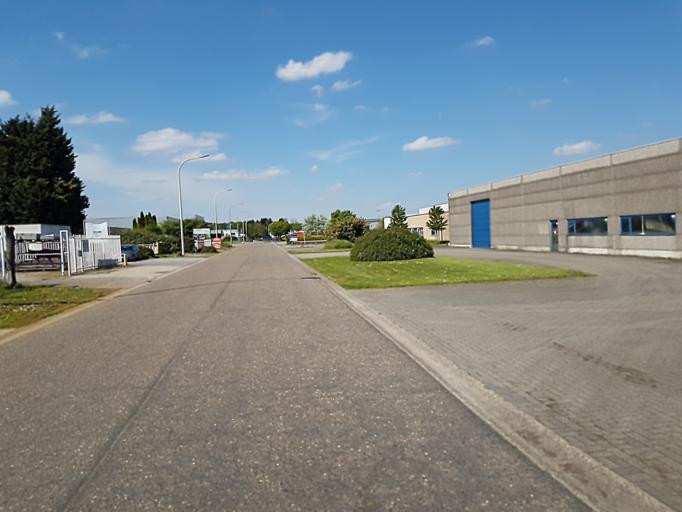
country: BE
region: Flanders
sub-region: Provincie Vlaams-Brabant
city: Aarschot
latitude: 50.9846
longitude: 4.8164
